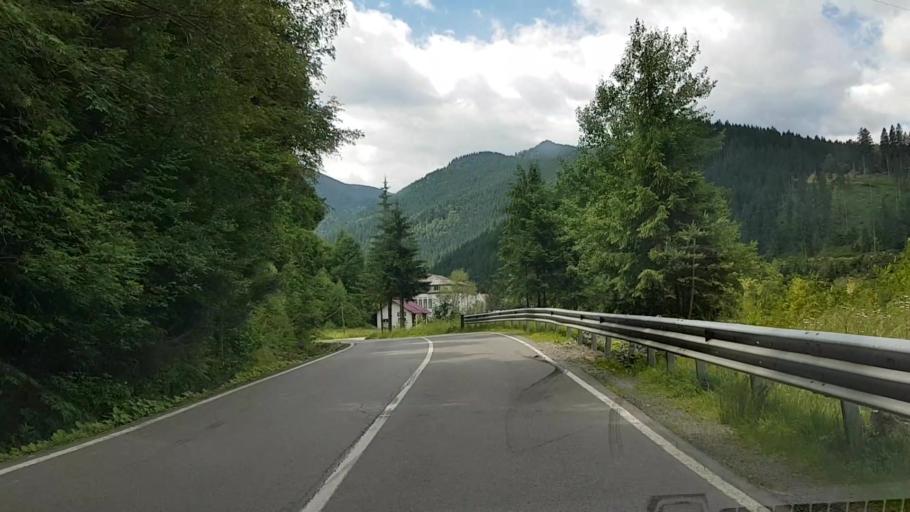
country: RO
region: Suceava
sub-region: Comuna Crucea
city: Crucea
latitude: 47.3519
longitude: 25.6146
